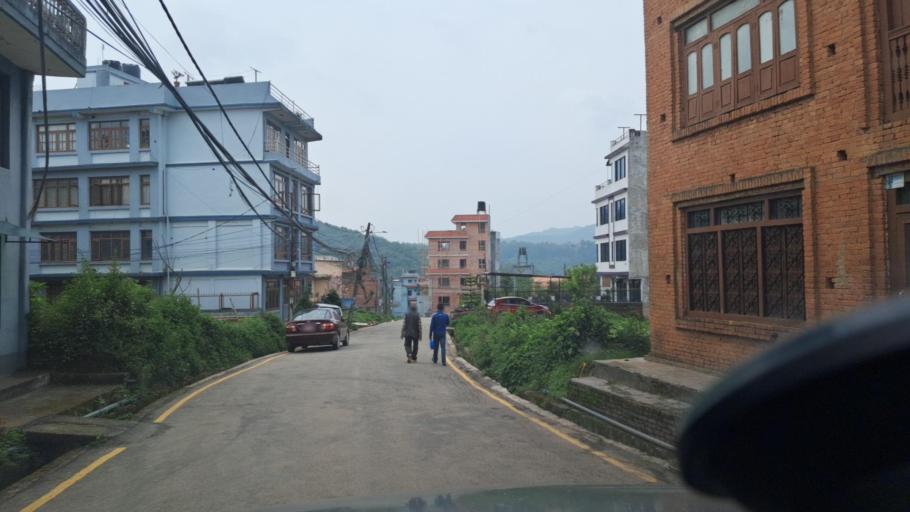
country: NP
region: Central Region
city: Banepa
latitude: 27.6163
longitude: 85.5531
